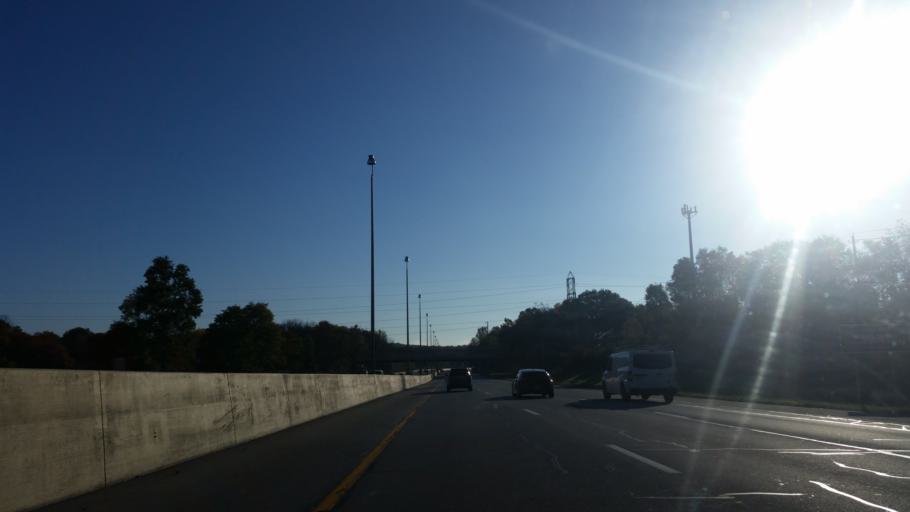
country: US
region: Ohio
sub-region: Summit County
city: Fairlawn
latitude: 41.1191
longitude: -81.6317
